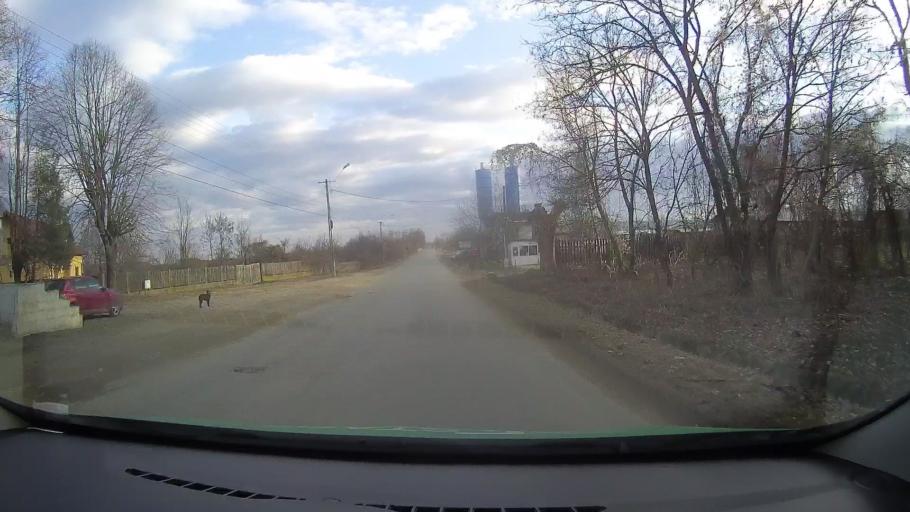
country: RO
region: Dambovita
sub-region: Municipiul Moreni
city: Moreni
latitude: 44.9609
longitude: 25.6572
